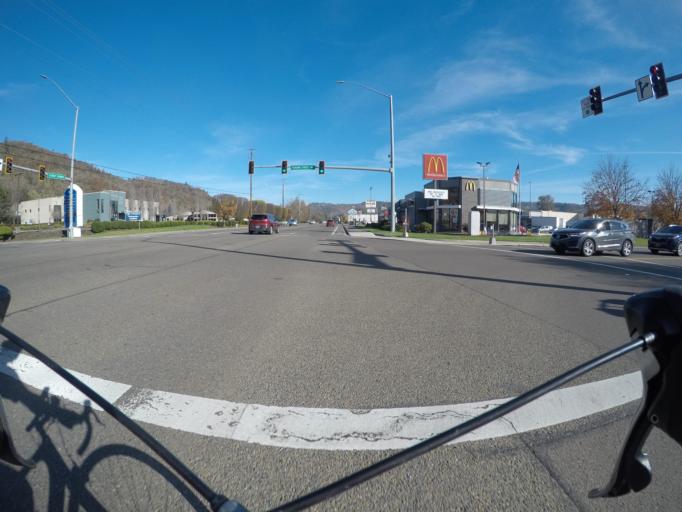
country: US
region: Oregon
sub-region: Douglas County
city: Roseburg
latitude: 43.2377
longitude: -123.3702
